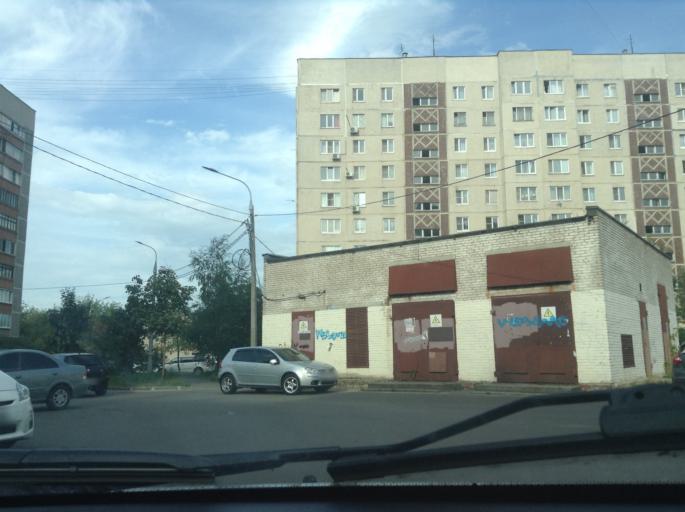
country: RU
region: Moskovskaya
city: Bykovo
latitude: 55.5961
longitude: 38.0906
